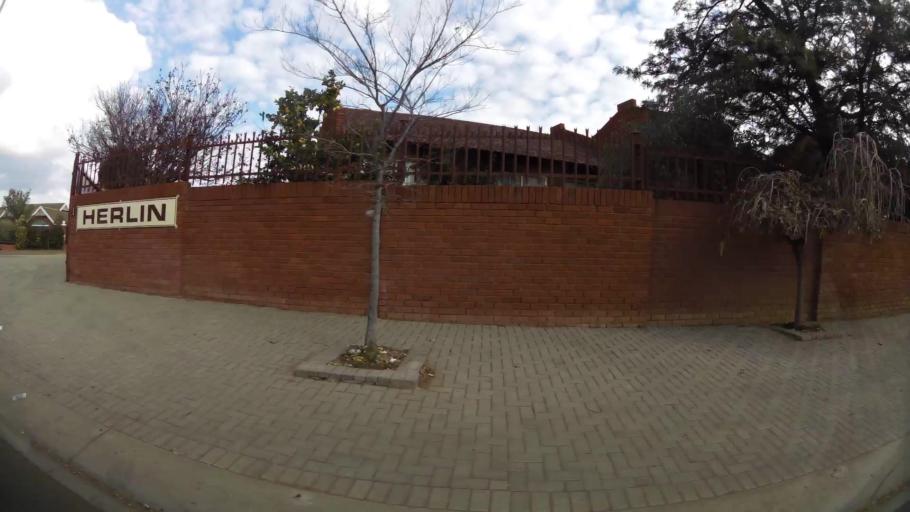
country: ZA
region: Orange Free State
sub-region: Mangaung Metropolitan Municipality
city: Bloemfontein
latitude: -29.0766
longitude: 26.1968
